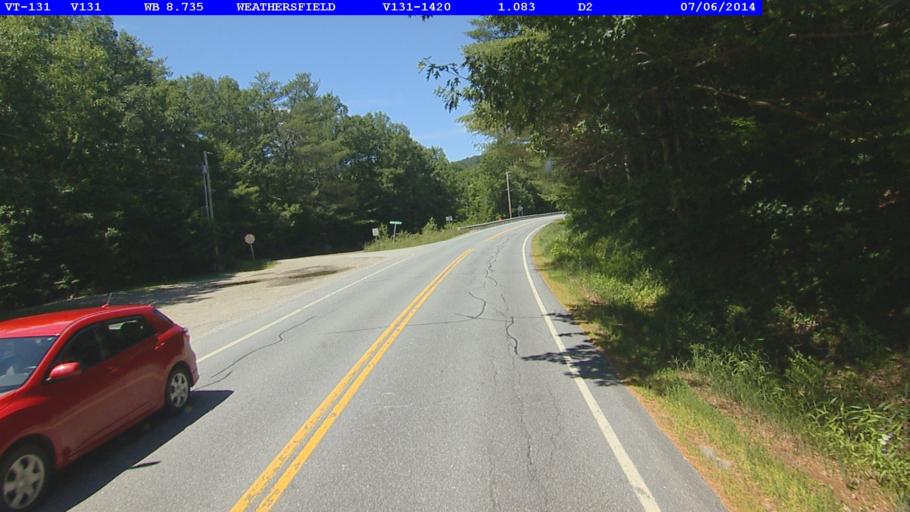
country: US
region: Vermont
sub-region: Windsor County
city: Springfield
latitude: 43.3989
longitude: -72.5201
